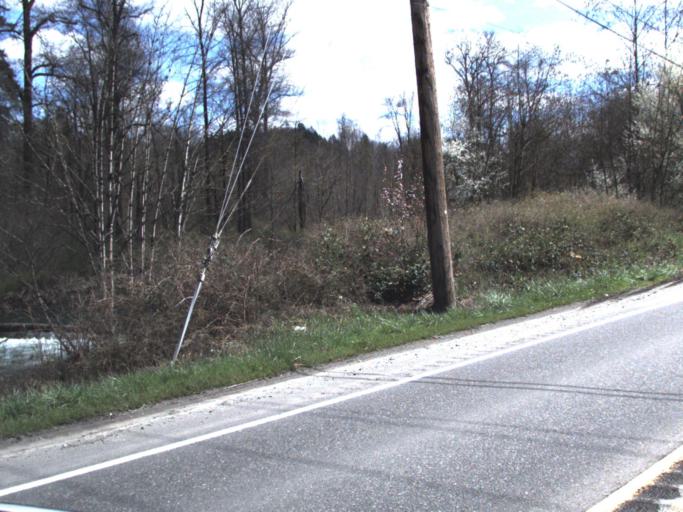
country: US
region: Washington
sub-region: King County
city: Maple Heights-Lake Desire
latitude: 47.4424
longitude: -122.0720
